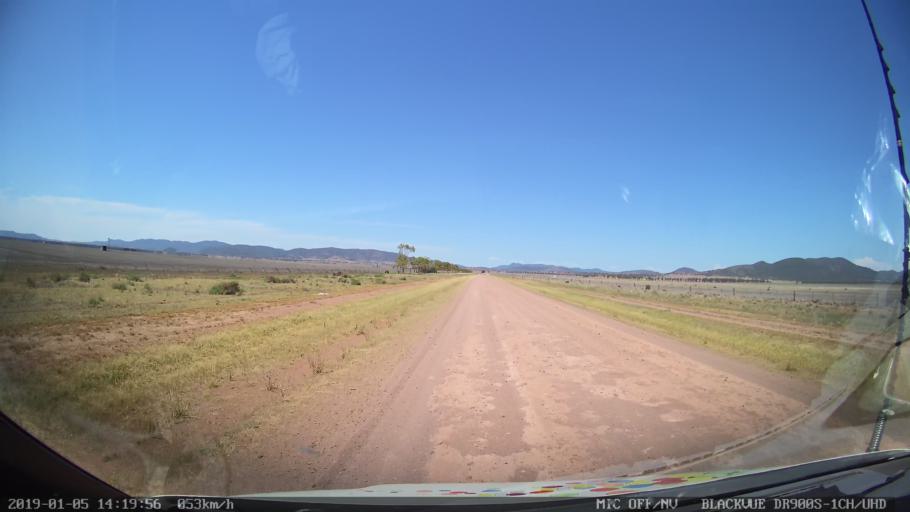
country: AU
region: New South Wales
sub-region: Liverpool Plains
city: Quirindi
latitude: -31.2499
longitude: 150.5003
